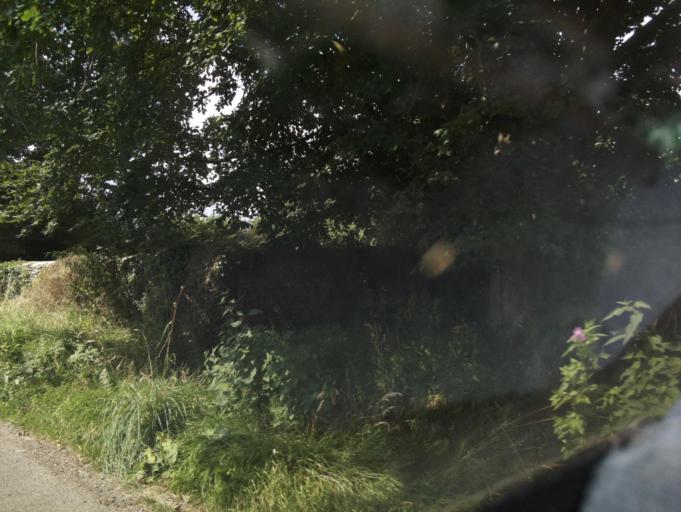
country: GB
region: England
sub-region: Wiltshire
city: Hankerton
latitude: 51.6123
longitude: -2.0468
